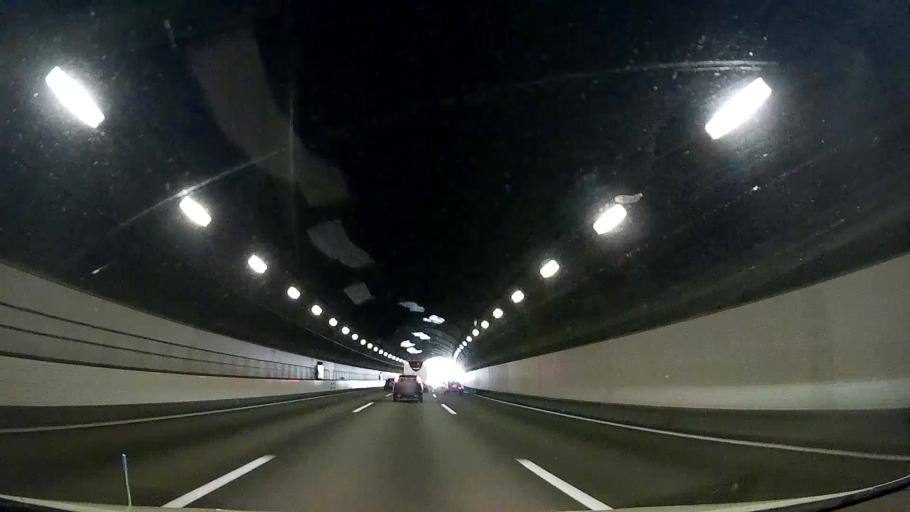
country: JP
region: Shizuoka
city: Gotemba
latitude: 35.3539
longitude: 138.9938
